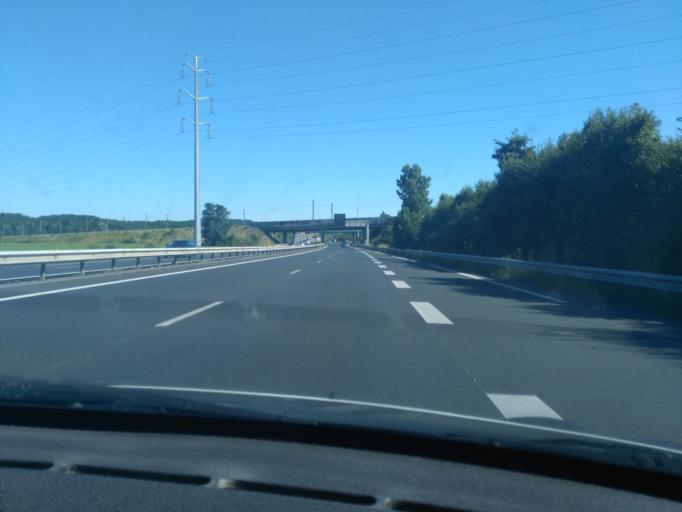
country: FR
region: Rhone-Alpes
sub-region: Departement du Rhone
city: Cailloux-sur-Fontaines
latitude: 45.8583
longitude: 4.9087
